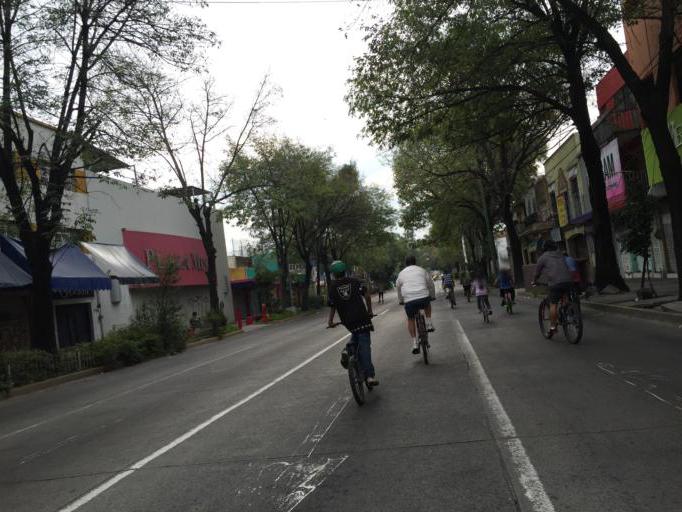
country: MX
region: Jalisco
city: Tlaquepaque
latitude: 20.6739
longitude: -103.3358
